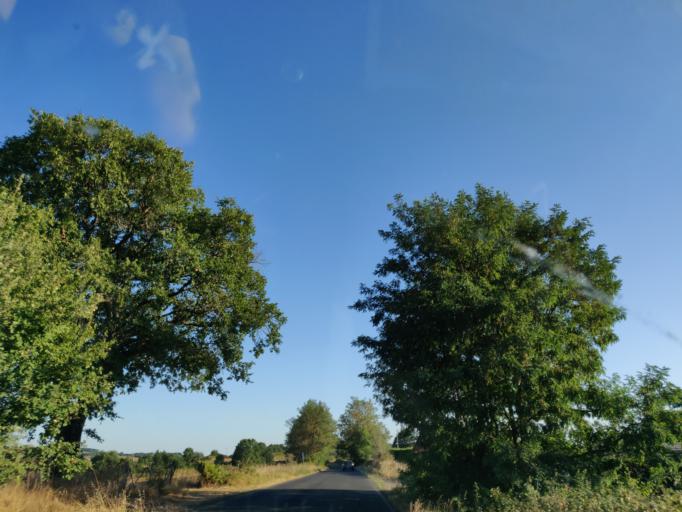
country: IT
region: Latium
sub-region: Provincia di Viterbo
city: Grotte di Castro
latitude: 42.7054
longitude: 11.8799
